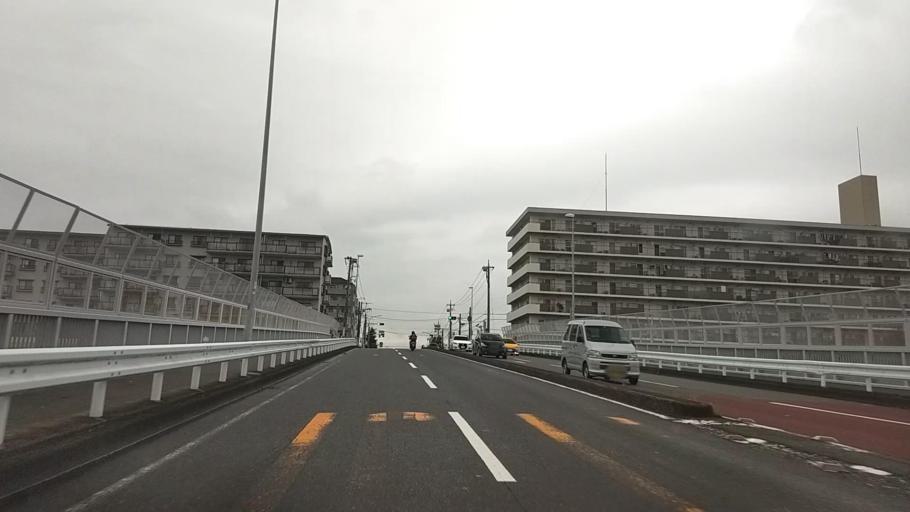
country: JP
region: Kanagawa
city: Kamakura
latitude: 35.3941
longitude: 139.5672
